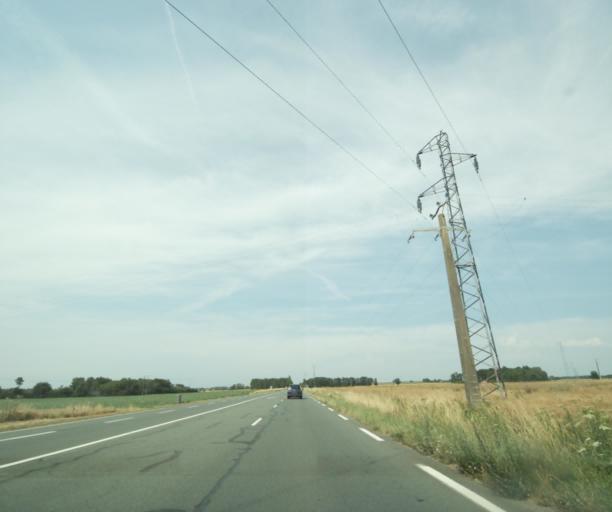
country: FR
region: Centre
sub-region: Departement d'Indre-et-Loire
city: Sorigny
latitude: 47.2089
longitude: 0.6756
